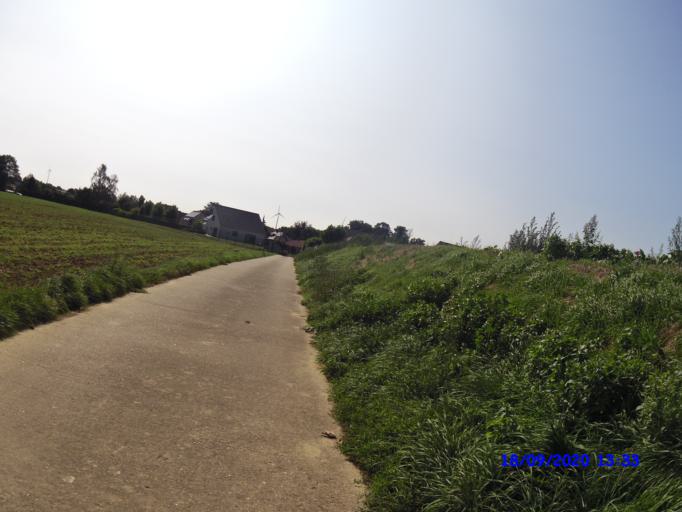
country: BE
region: Flanders
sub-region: Provincie Limburg
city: Gingelom
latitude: 50.7266
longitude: 5.1322
